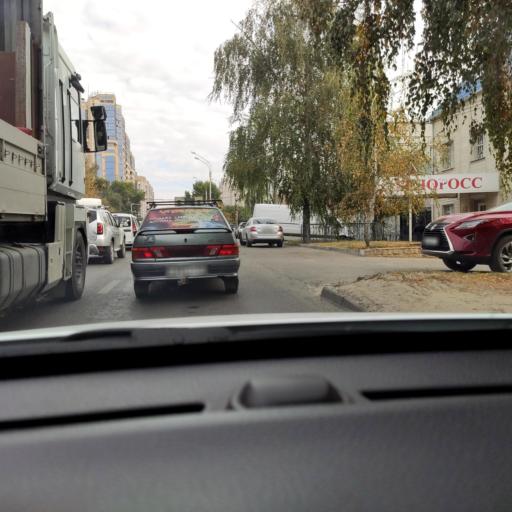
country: RU
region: Voronezj
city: Voronezh
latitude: 51.6951
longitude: 39.1804
